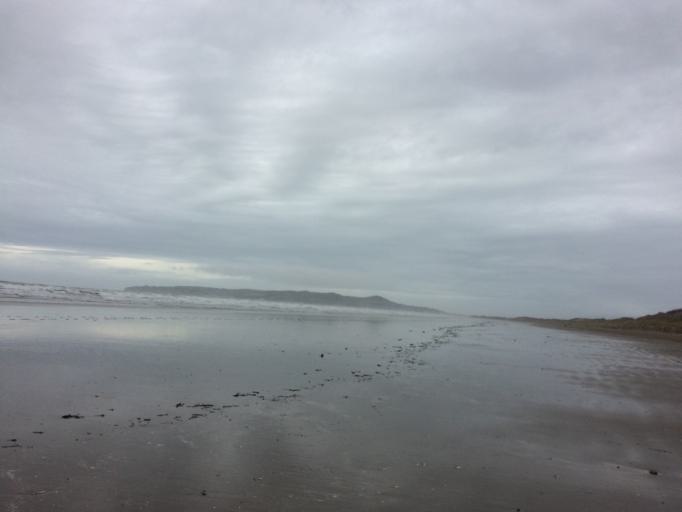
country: IE
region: Leinster
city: Portmarnock
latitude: 53.4276
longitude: -6.1232
